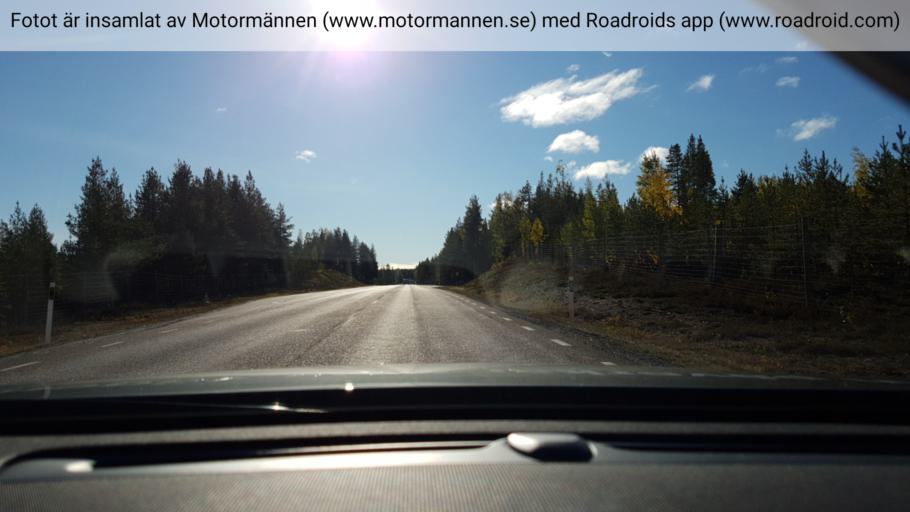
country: SE
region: Vaesterbotten
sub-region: Skelleftea Kommun
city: Burea
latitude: 64.5950
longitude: 21.2096
